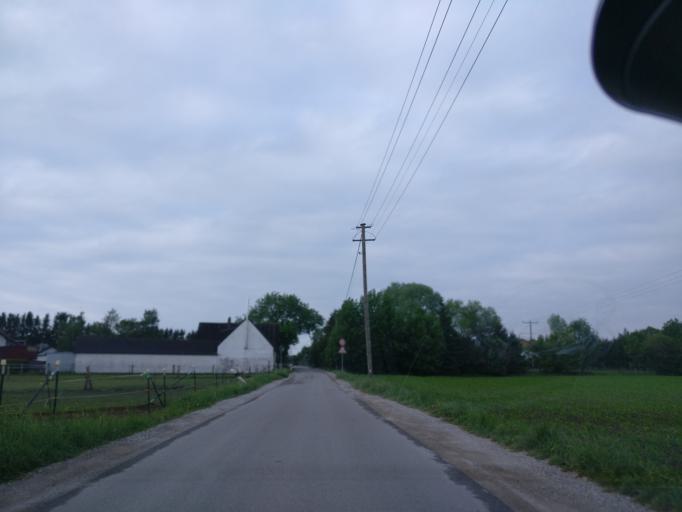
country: DE
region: Bavaria
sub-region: Upper Bavaria
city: Karlsfeld
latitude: 48.1955
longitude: 11.4306
